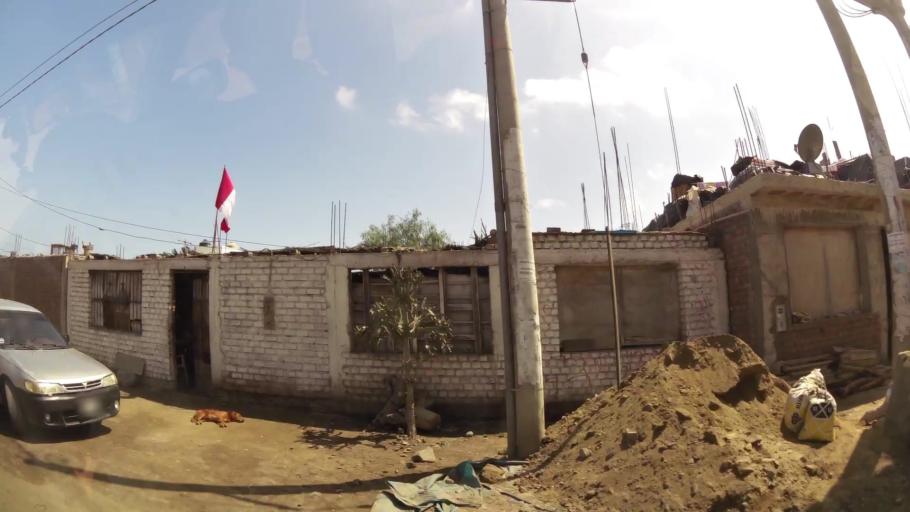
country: PE
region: Lima
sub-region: Provincia de Canete
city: Mala
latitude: -12.6682
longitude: -76.6426
